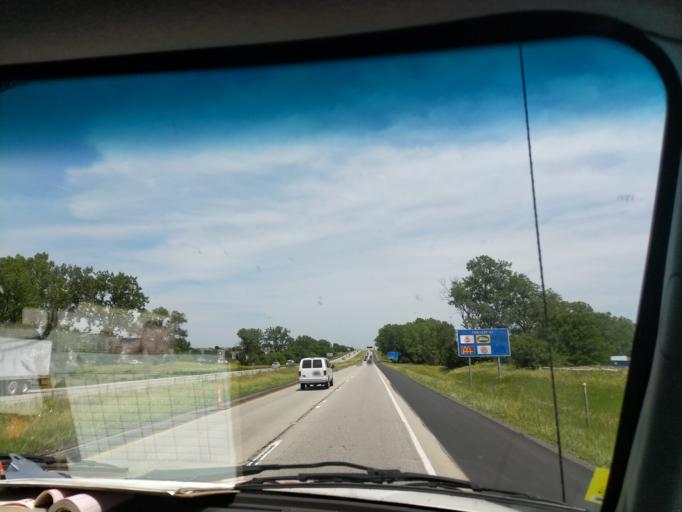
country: US
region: Iowa
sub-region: Dallas County
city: Waukee
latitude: 41.5808
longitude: -93.8309
